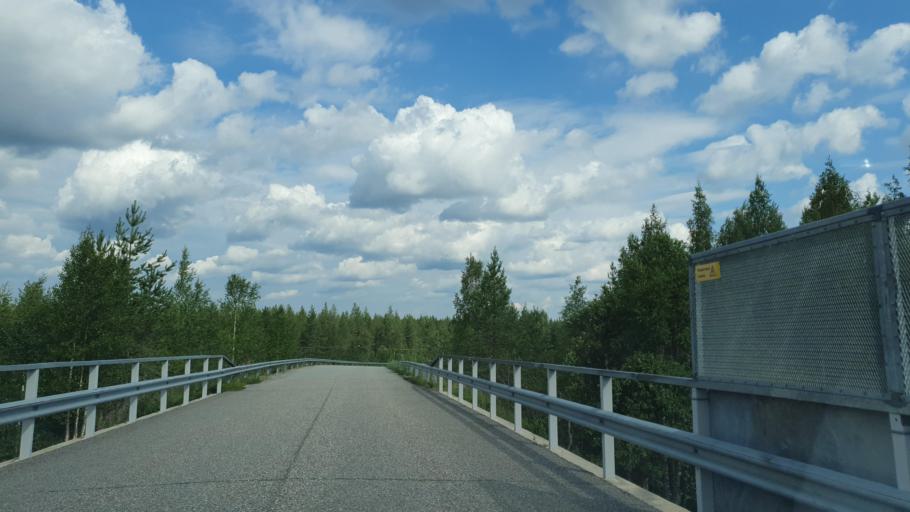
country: FI
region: Kainuu
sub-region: Kehys-Kainuu
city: Kuhmo
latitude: 64.4928
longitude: 29.5956
